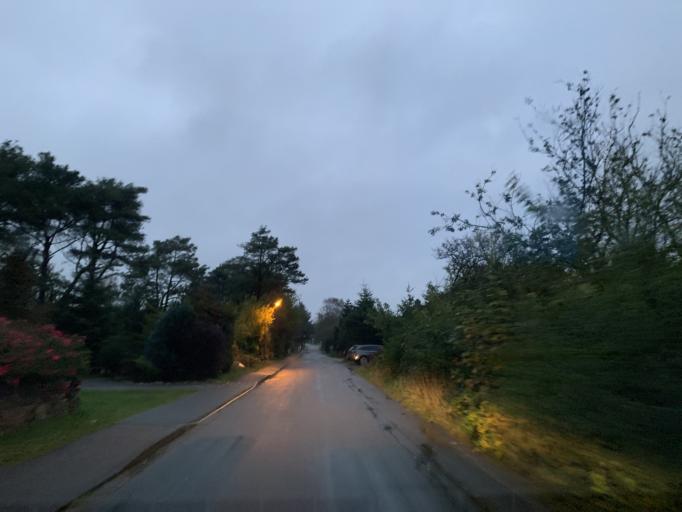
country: DE
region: Schleswig-Holstein
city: Nebel
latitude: 54.6475
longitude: 8.3446
